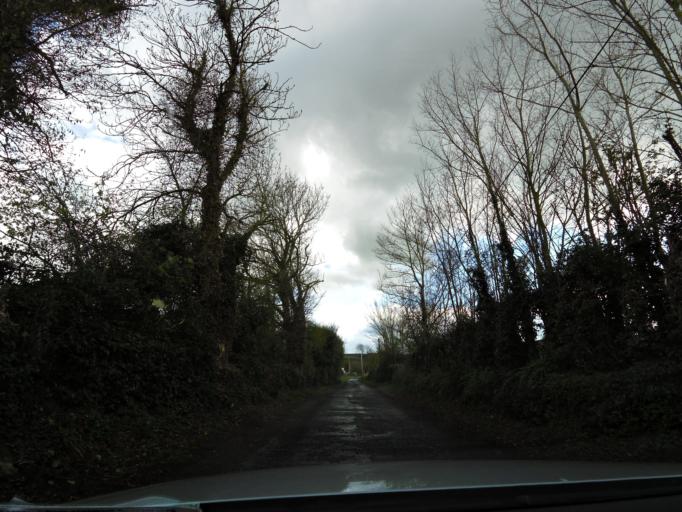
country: IE
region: Leinster
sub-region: Laois
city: Rathdowney
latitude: 52.8156
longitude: -7.4726
